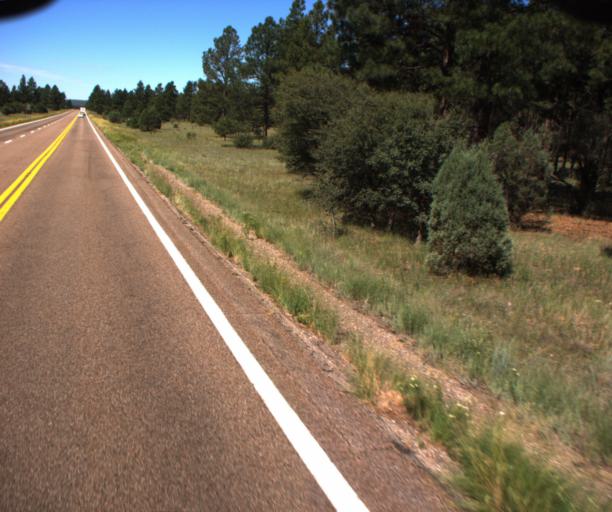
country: US
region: Arizona
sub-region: Navajo County
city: Lake of the Woods
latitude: 34.1173
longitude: -110.1340
